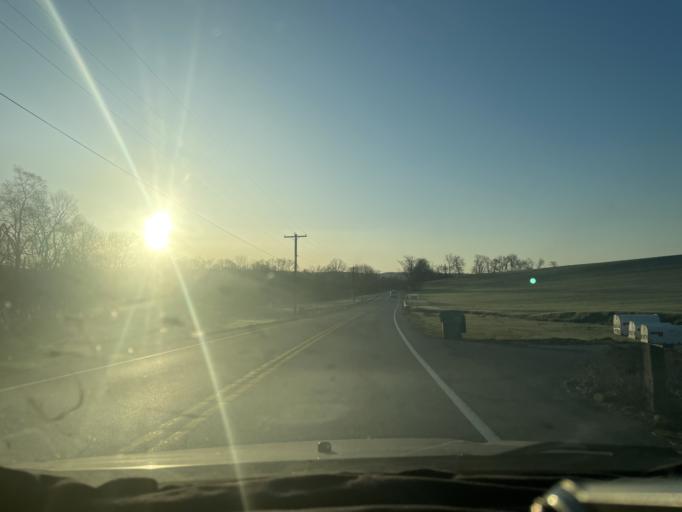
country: US
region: Maryland
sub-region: Frederick County
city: Adamstown
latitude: 39.2533
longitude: -77.4495
